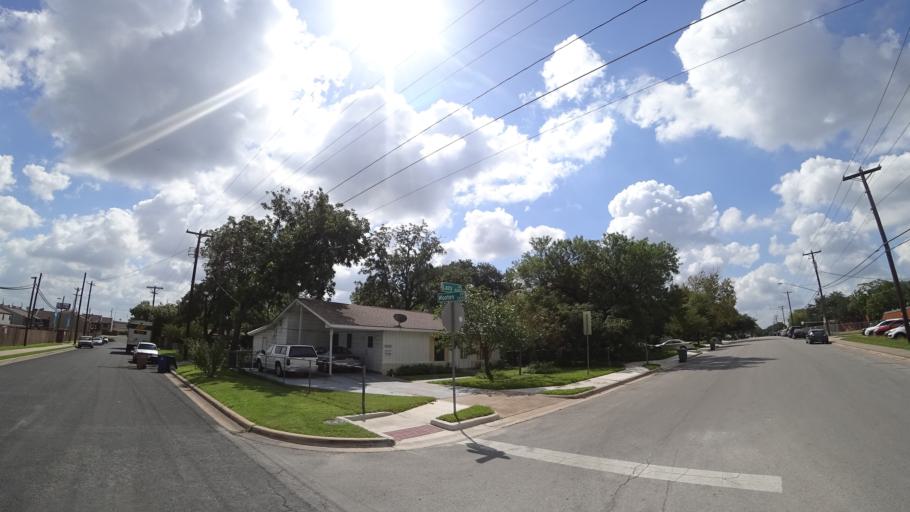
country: US
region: Texas
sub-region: Travis County
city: Austin
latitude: 30.3544
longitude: -97.7181
